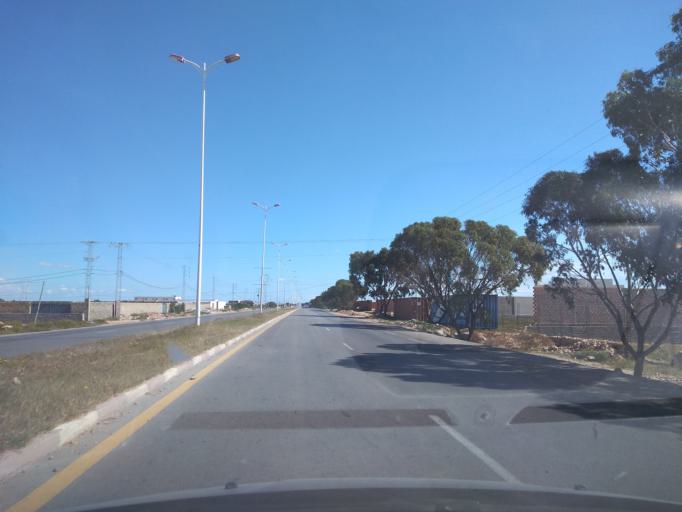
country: TN
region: Safaqis
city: Sfax
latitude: 34.8175
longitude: 10.7026
